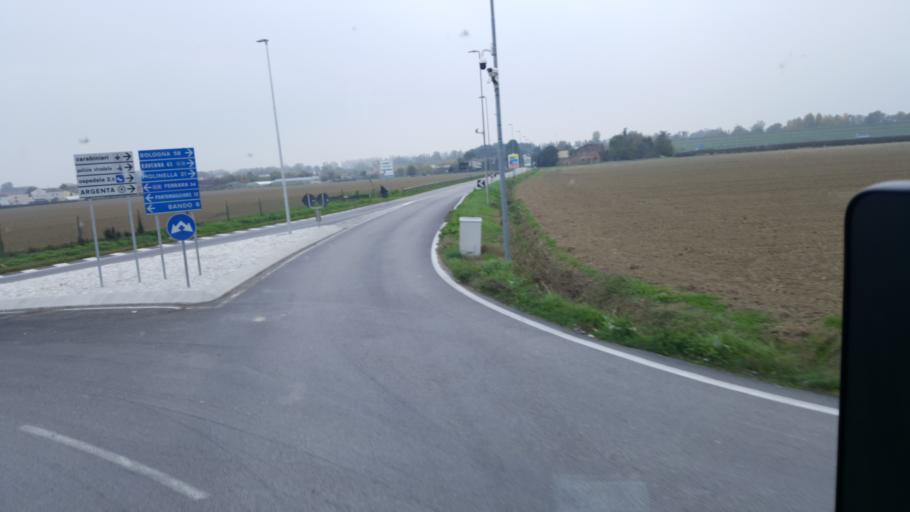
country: IT
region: Emilia-Romagna
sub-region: Provincia di Ferrara
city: Argenta
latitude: 44.6267
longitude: 11.8248
